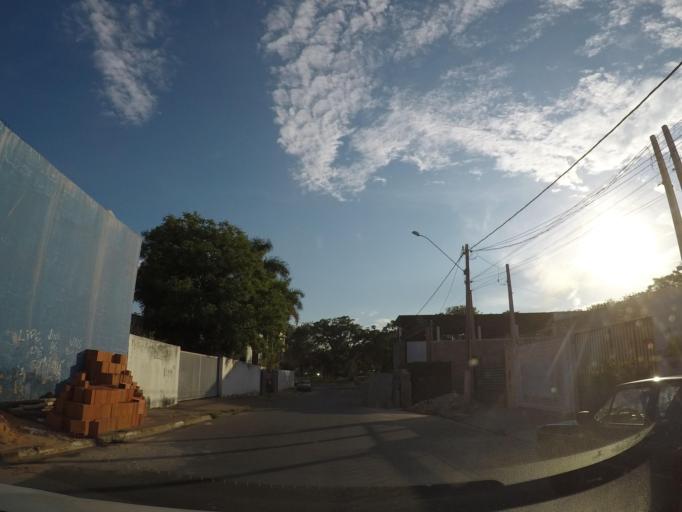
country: BR
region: Sao Paulo
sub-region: Sumare
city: Sumare
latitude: -22.8165
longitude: -47.2638
